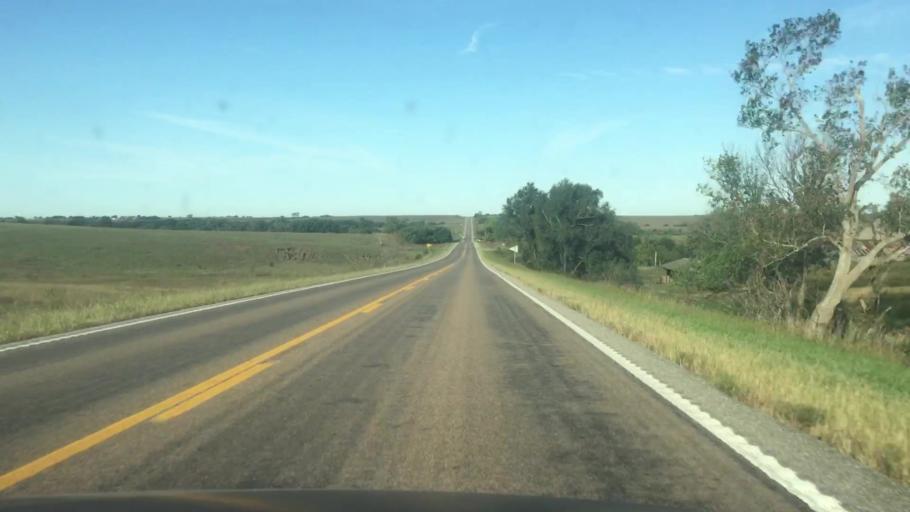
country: US
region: Nebraska
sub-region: Thayer County
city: Hebron
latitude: 40.1473
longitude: -97.5119
